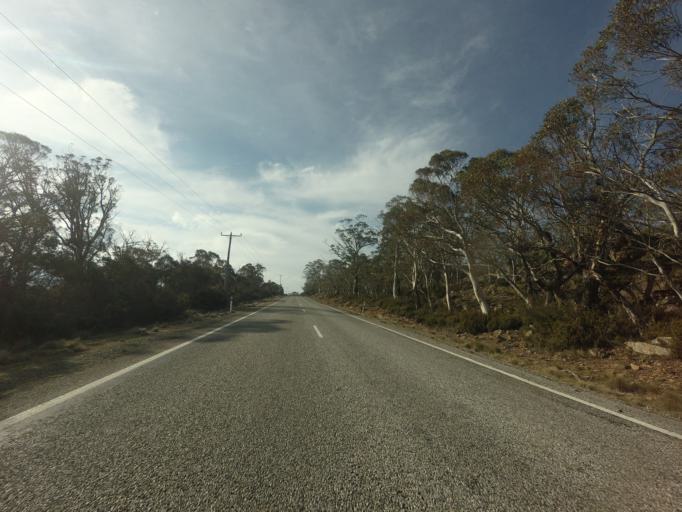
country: AU
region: Tasmania
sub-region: Meander Valley
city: Deloraine
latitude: -41.9902
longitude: 146.7088
